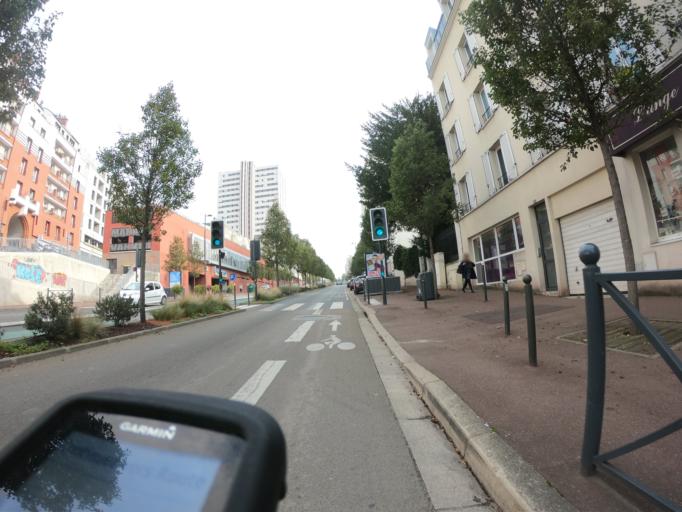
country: FR
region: Ile-de-France
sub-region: Departement des Hauts-de-Seine
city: Vanves
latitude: 48.8215
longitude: 2.2871
